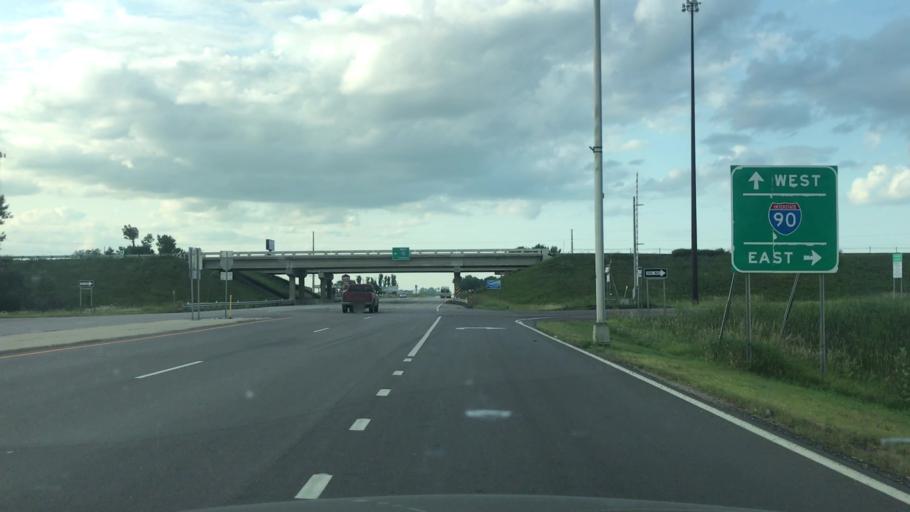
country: US
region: Minnesota
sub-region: Nobles County
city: Worthington
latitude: 43.6367
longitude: -95.5934
